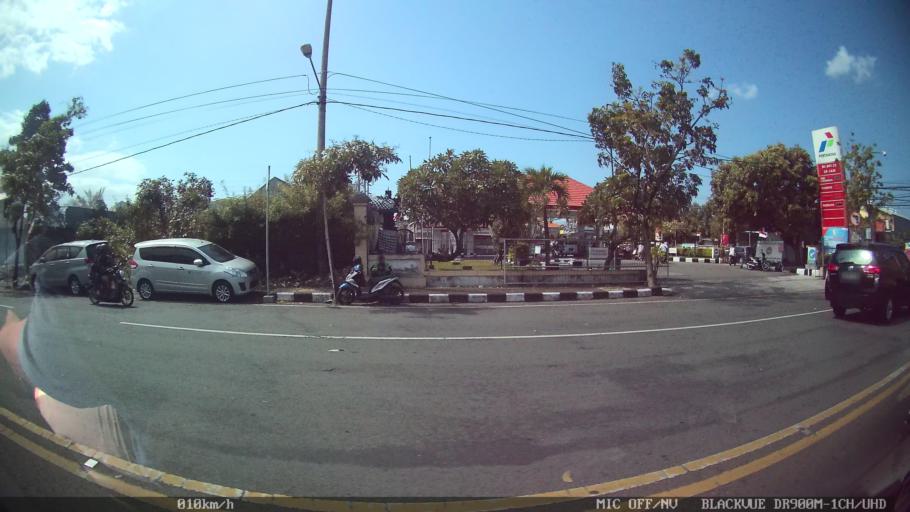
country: ID
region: Bali
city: Karyadharma
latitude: -8.6867
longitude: 115.1864
